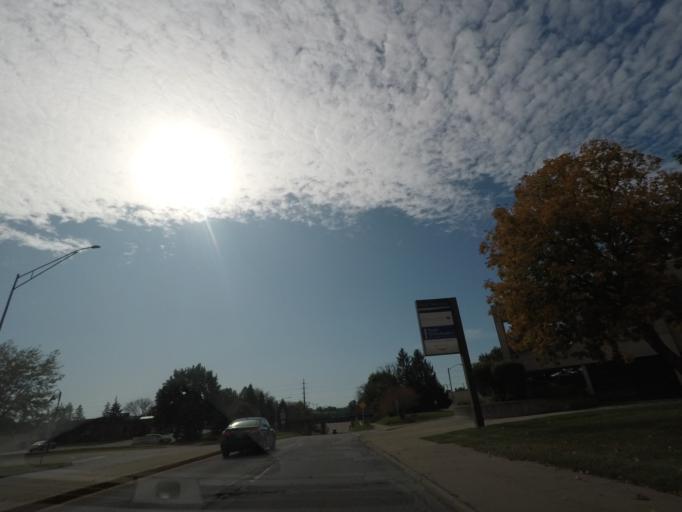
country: US
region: Iowa
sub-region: Story County
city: Ames
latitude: 42.0261
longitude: -93.6203
